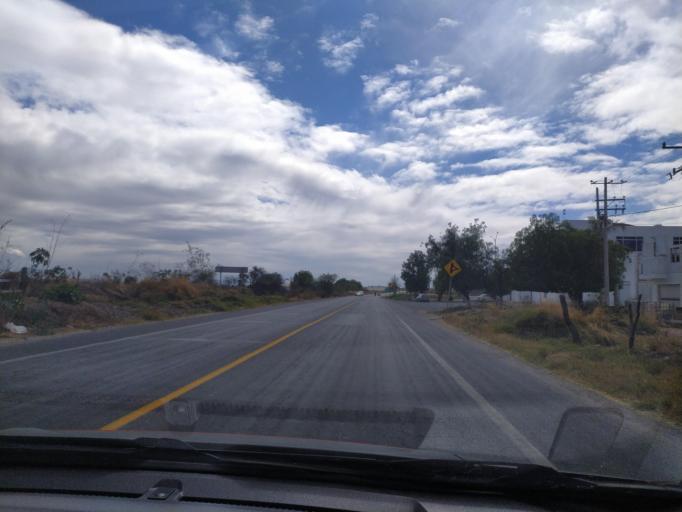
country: LA
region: Oudomxai
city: Muang La
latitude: 21.0148
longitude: 101.8278
